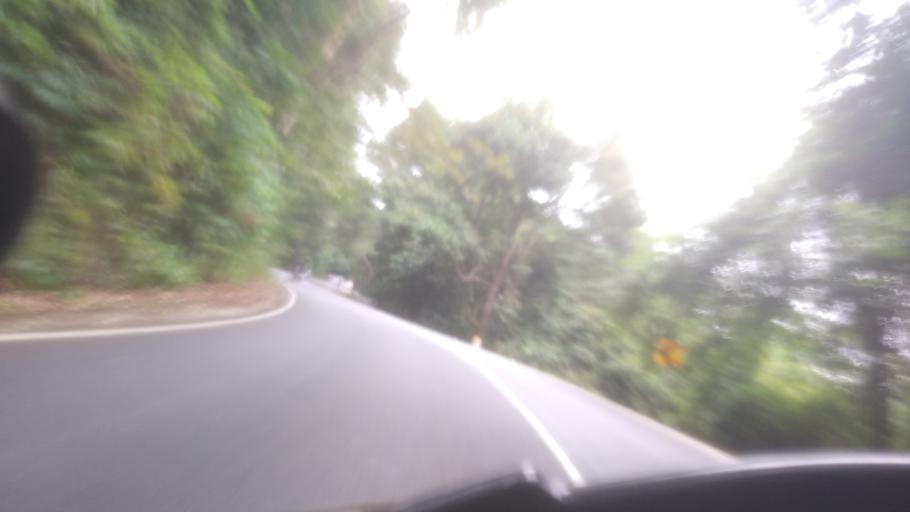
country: IN
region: Kerala
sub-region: Idukki
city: Kuttampuzha
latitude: 10.0575
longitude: 76.8058
